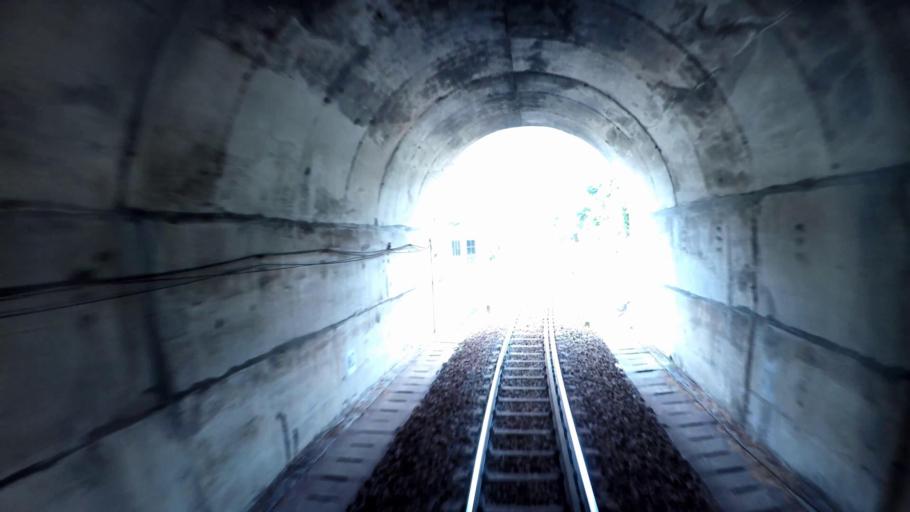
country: VN
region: Da Nang
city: Lien Chieu
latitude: 16.1743
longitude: 108.1390
